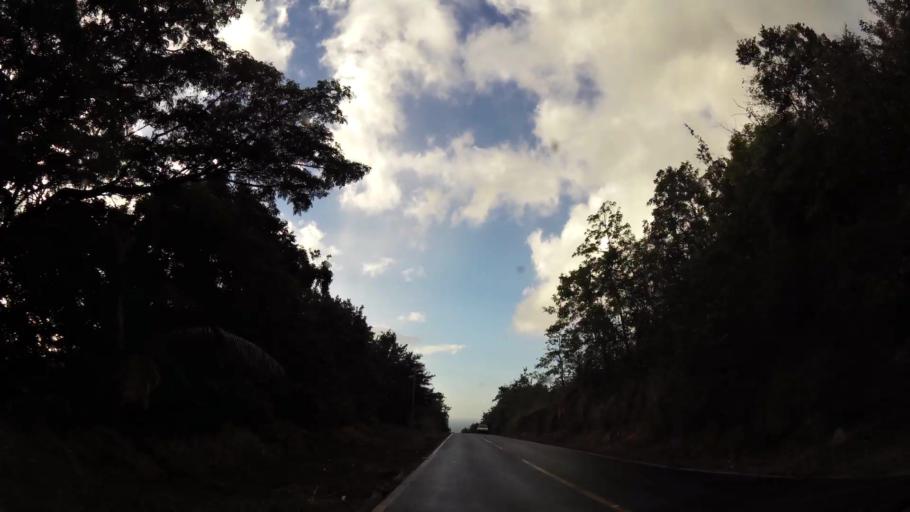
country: DM
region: Saint Peter
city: Colihaut
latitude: 15.5253
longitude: -61.4627
